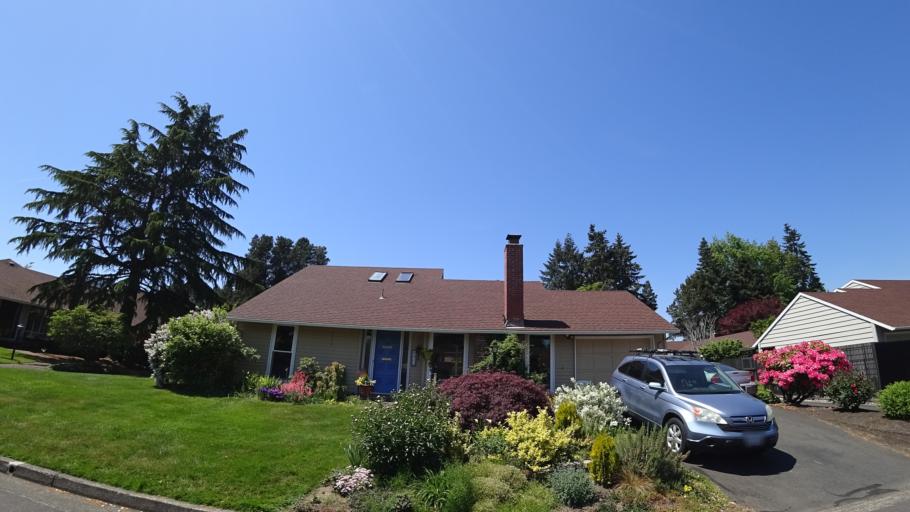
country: US
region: Oregon
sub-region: Washington County
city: Beaverton
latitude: 45.4844
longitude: -122.8242
